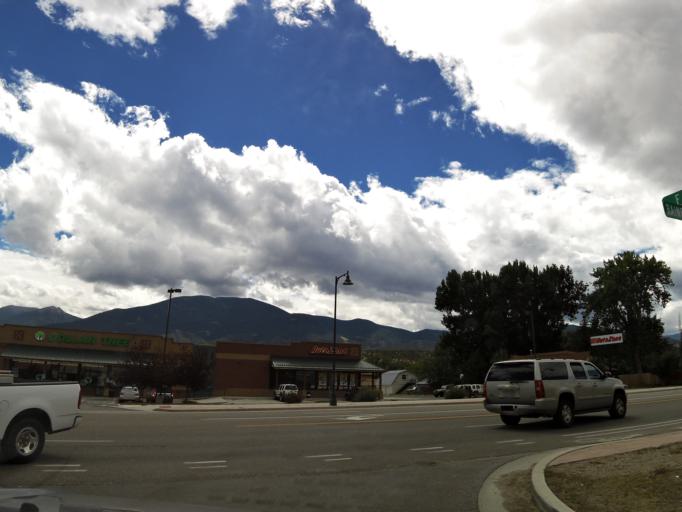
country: US
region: Colorado
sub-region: Chaffee County
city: Salida
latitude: 38.5243
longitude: -106.0036
